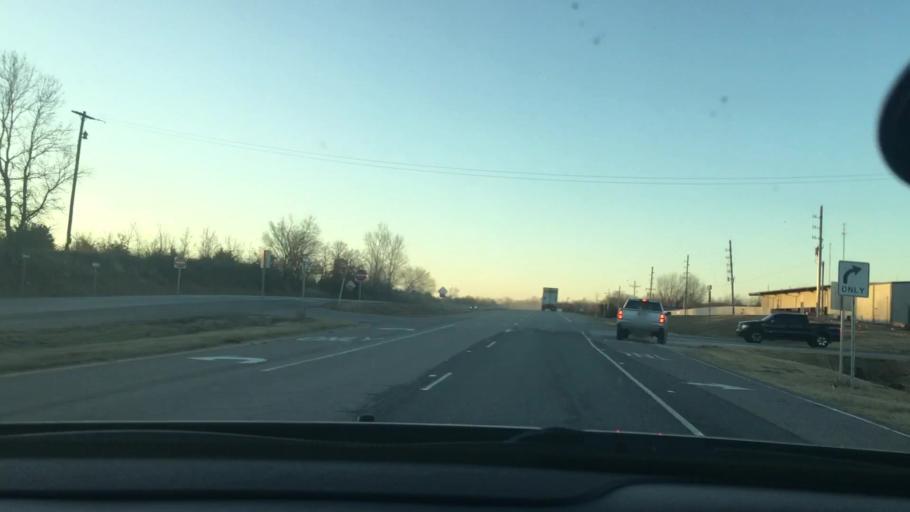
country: US
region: Oklahoma
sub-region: Pontotoc County
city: Ada
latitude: 34.7385
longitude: -96.7090
